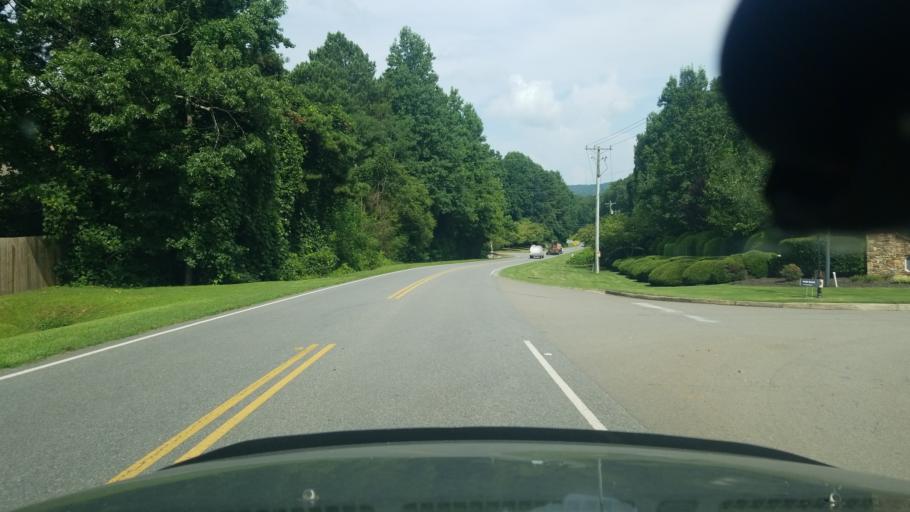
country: US
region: Georgia
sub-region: Dawson County
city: Dawsonville
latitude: 34.3133
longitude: -84.0759
